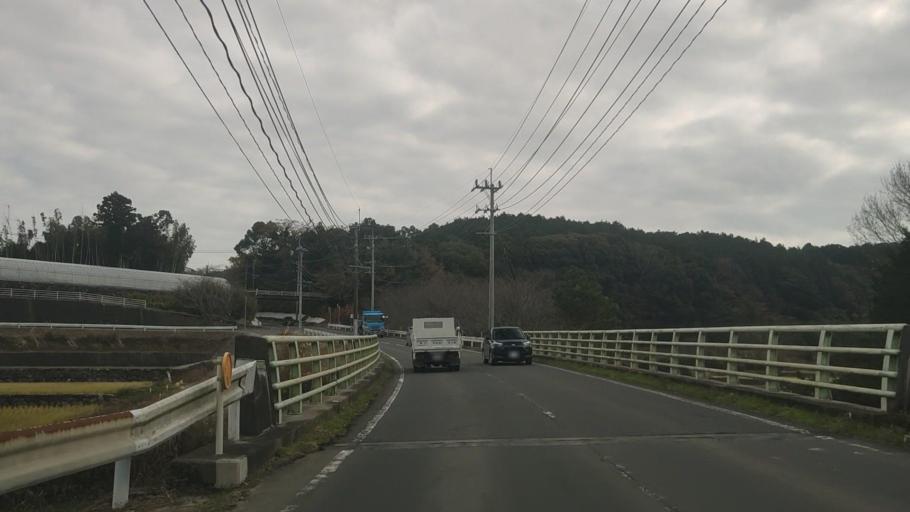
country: JP
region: Nagasaki
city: Shimabara
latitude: 32.8491
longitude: 130.2776
